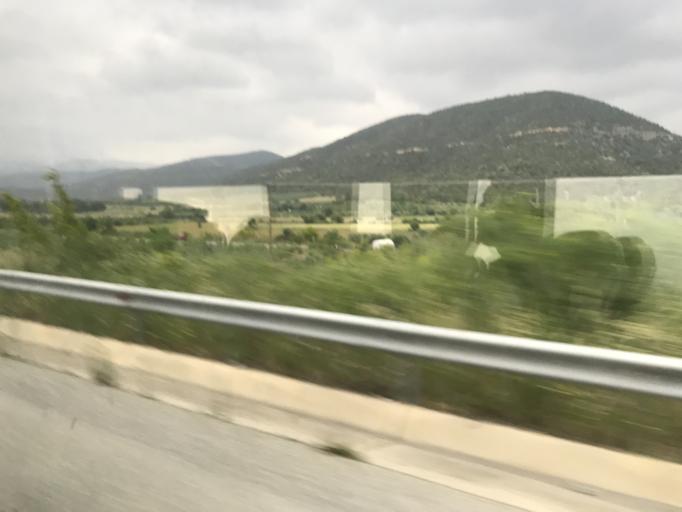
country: GR
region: East Macedonia and Thrace
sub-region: Nomos Rodopis
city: Iasmos
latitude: 41.1192
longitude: 25.0928
